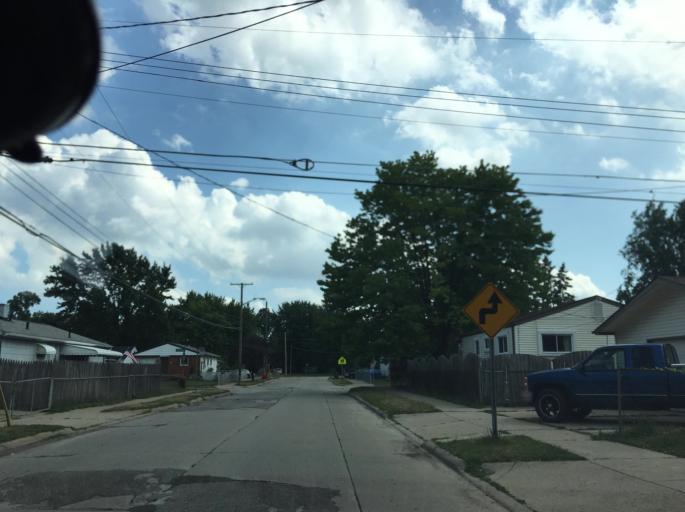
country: US
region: Michigan
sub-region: Macomb County
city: Clinton
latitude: 42.5521
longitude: -82.9102
